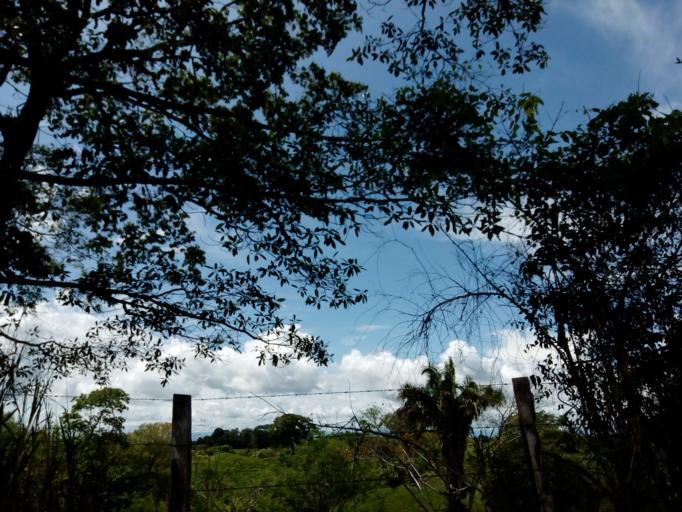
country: CO
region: Boyaca
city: Puerto Boyaca
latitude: 5.9698
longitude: -74.4376
